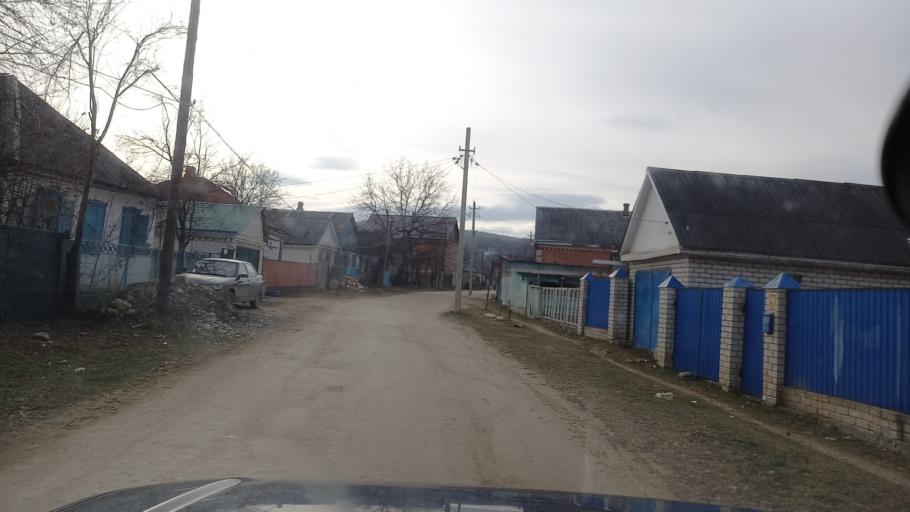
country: RU
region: Adygeya
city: Kamennomostskiy
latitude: 44.2907
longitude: 40.1909
